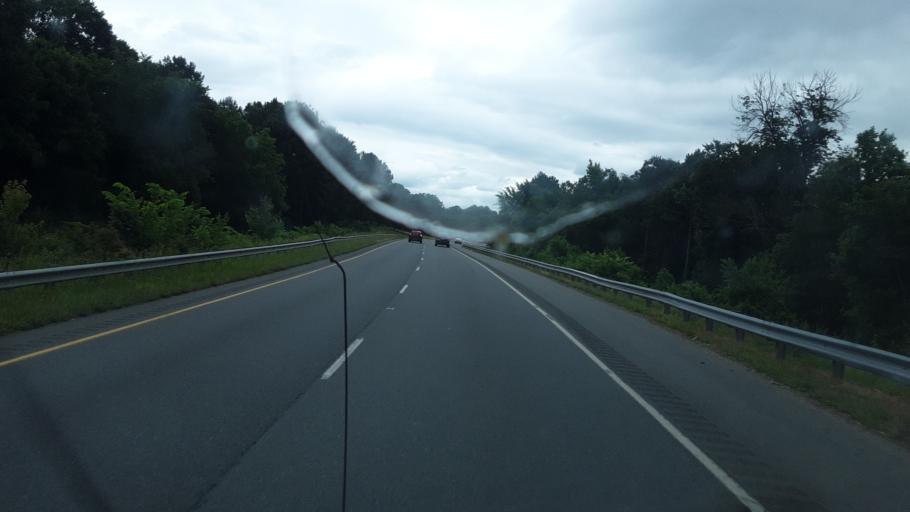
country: US
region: North Carolina
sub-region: Forsyth County
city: Clemmons
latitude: 36.0699
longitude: -80.3237
